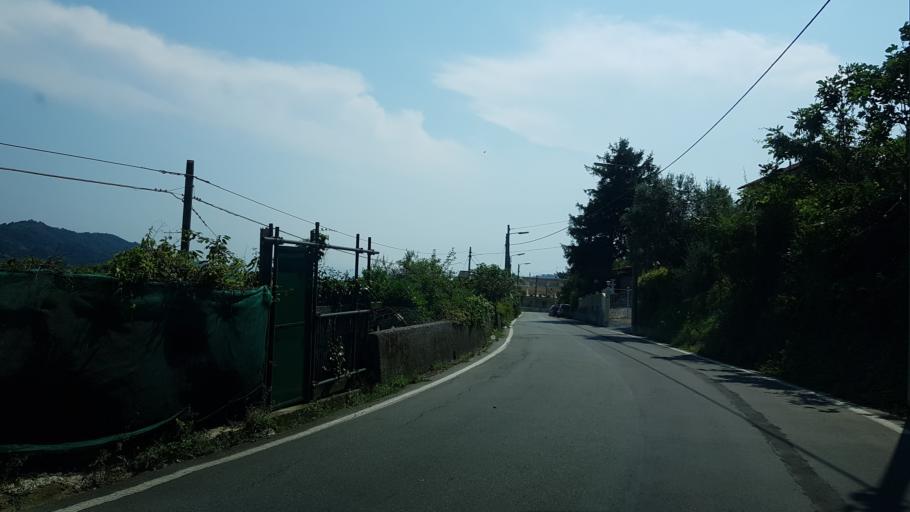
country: IT
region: Liguria
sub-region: Provincia di Genova
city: Genoa
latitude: 44.4490
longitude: 8.9034
